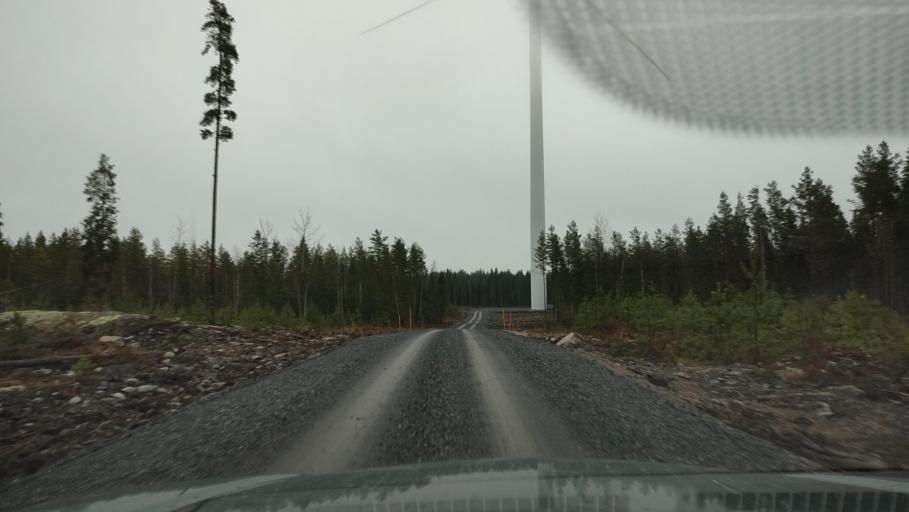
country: FI
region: Southern Ostrobothnia
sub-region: Suupohja
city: Karijoki
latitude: 62.1591
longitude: 21.5947
